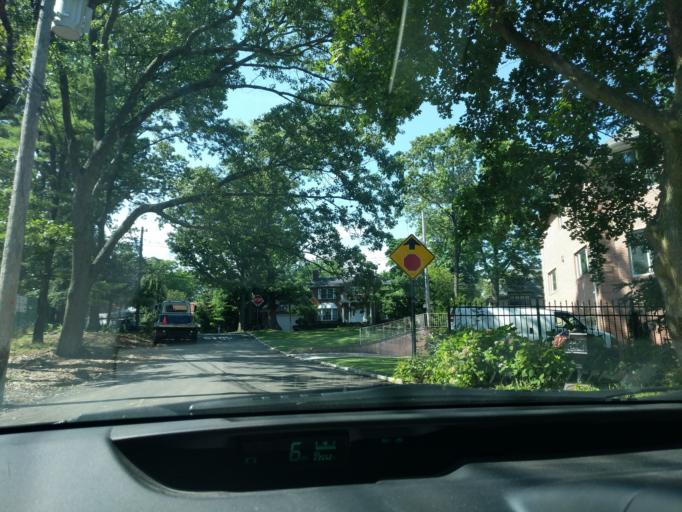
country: US
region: New York
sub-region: Richmond County
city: Staten Island
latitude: 40.6054
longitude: -74.0984
